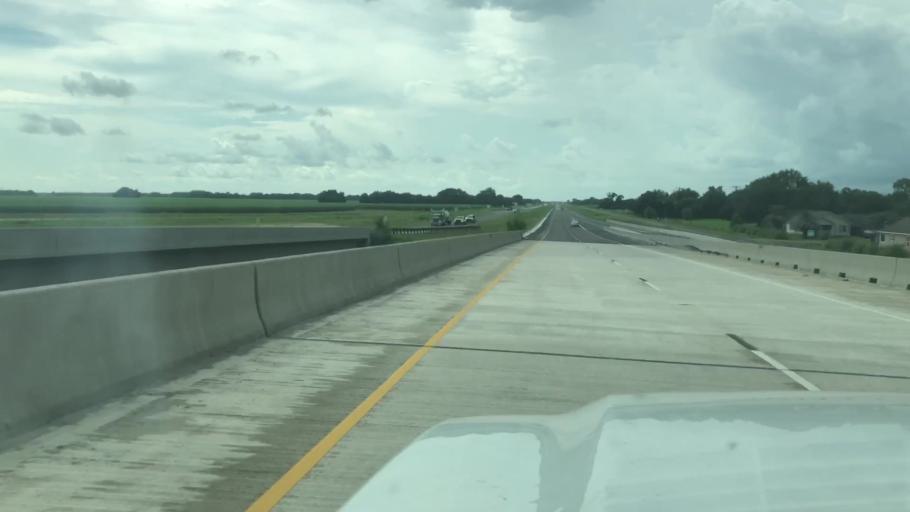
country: US
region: Louisiana
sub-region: Iberia Parish
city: Jeanerette
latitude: 29.8676
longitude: -91.6355
